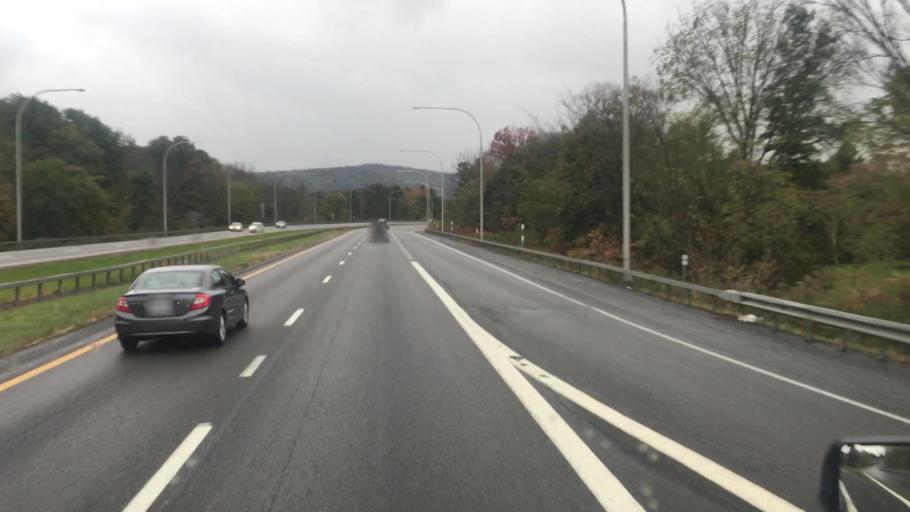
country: US
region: New York
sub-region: Broome County
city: Endicott
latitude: 42.0952
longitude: -76.0334
